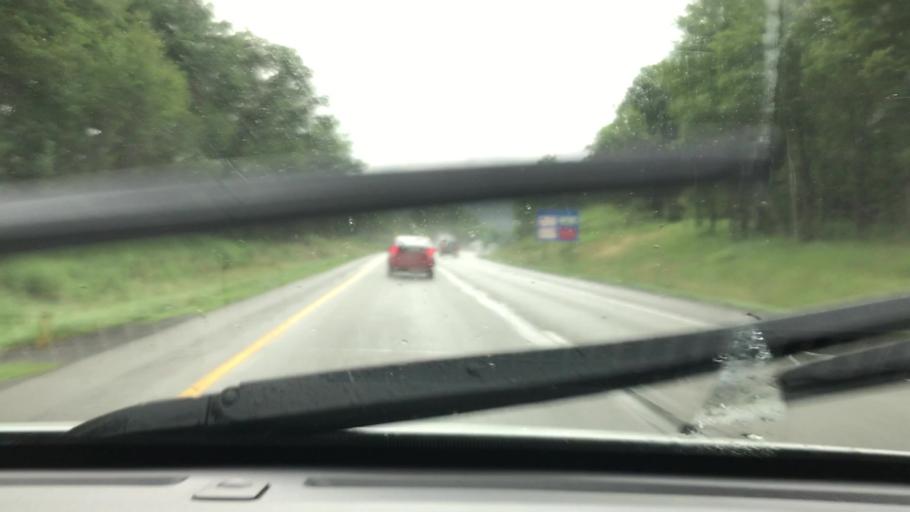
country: US
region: Pennsylvania
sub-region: Clearfield County
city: Clearfield
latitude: 41.0301
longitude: -78.3750
